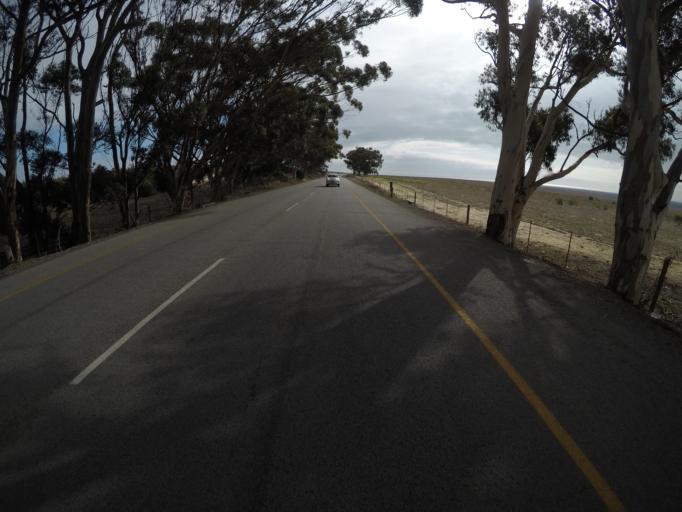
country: ZA
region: Western Cape
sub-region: City of Cape Town
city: Sunset Beach
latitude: -33.7229
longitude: 18.5032
